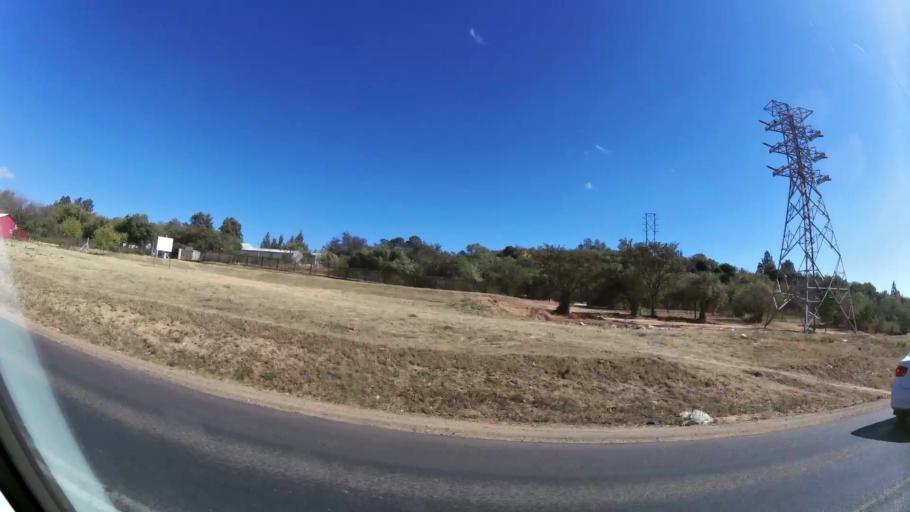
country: ZA
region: Gauteng
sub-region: City of Johannesburg Metropolitan Municipality
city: Midrand
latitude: -25.9661
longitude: 28.0805
